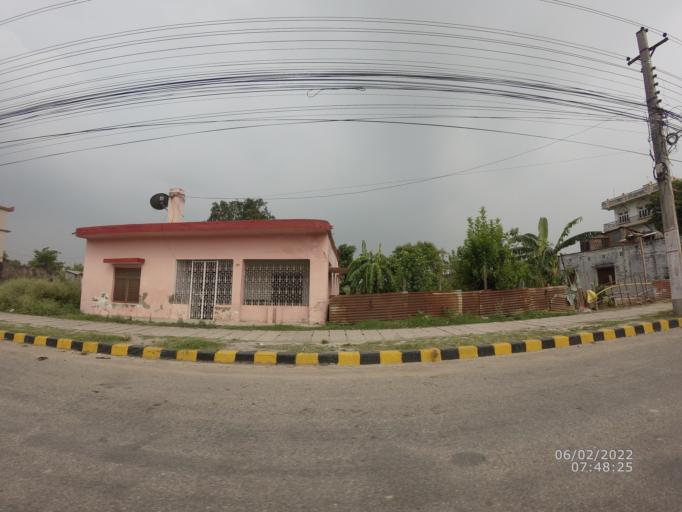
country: NP
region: Western Region
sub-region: Lumbini Zone
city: Bhairahawa
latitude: 27.5264
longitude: 83.4558
